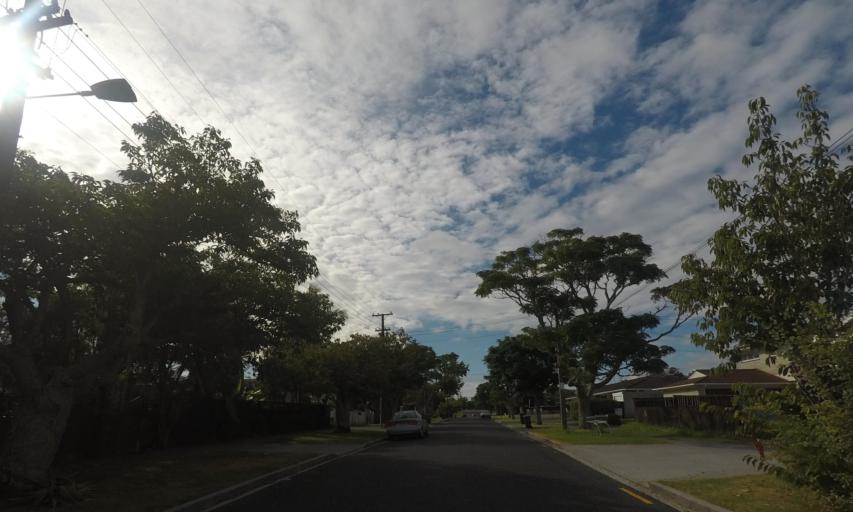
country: NZ
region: Auckland
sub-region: Auckland
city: Auckland
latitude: -36.8901
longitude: 174.7295
